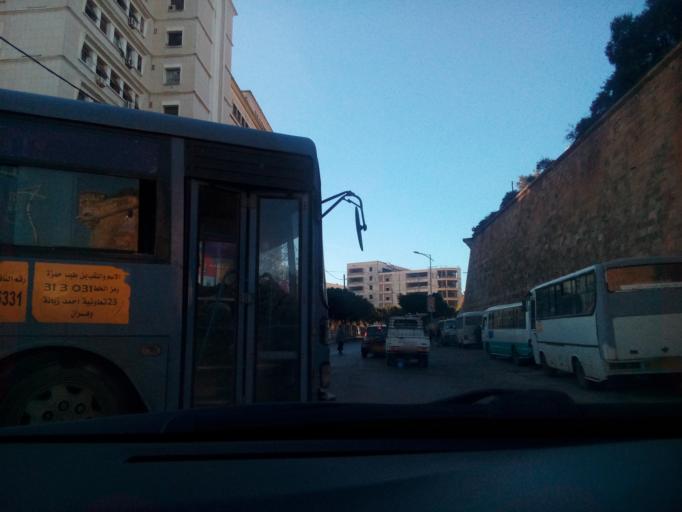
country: DZ
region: Oran
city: Oran
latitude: 35.7057
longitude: -0.6472
